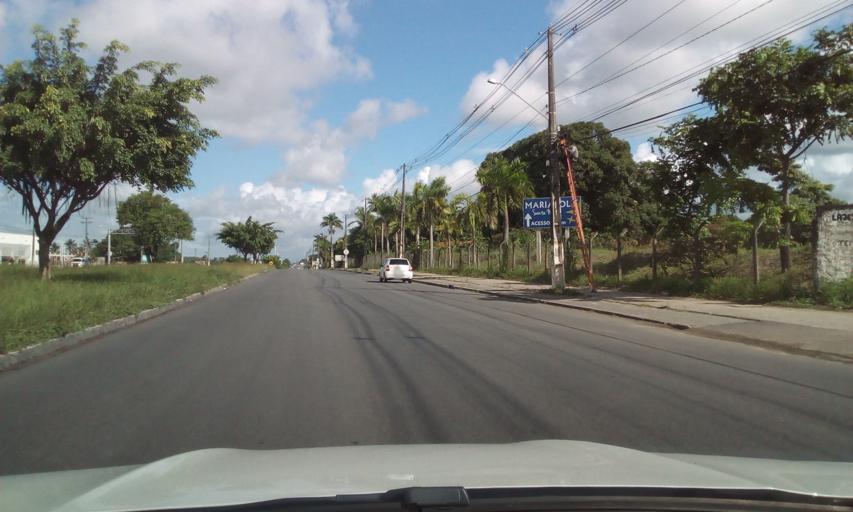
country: BR
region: Pernambuco
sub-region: Igarassu
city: Igarassu
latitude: -7.8510
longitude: -34.9095
